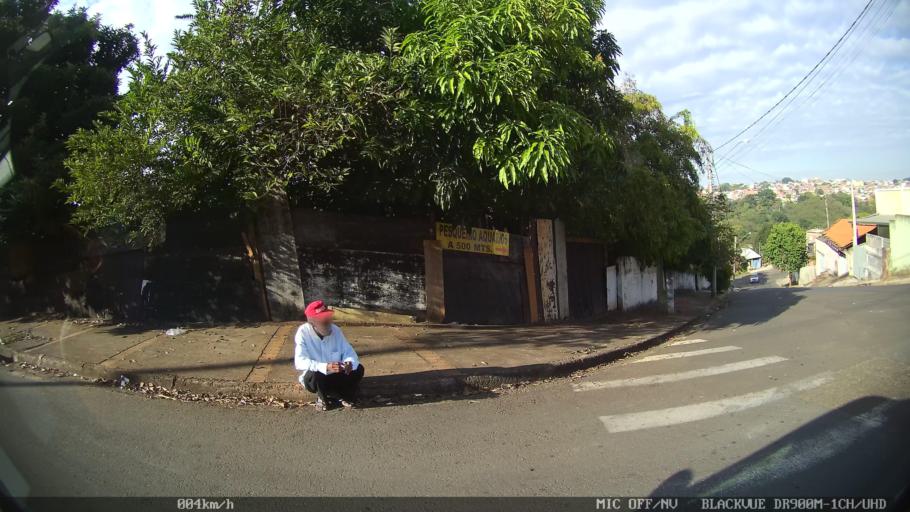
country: BR
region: Sao Paulo
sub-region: Americana
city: Americana
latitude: -22.7282
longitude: -47.3727
